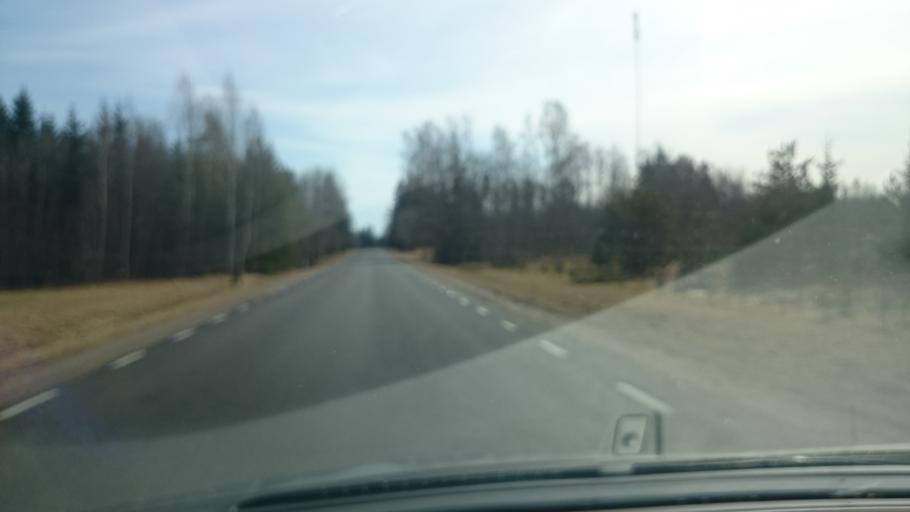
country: EE
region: Paernumaa
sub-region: Vaendra vald (alev)
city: Vandra
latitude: 58.6309
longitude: 24.9181
